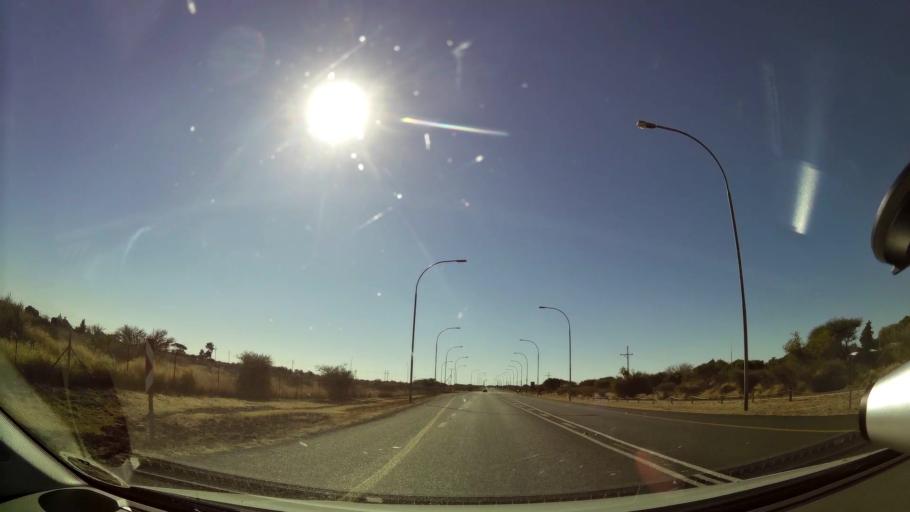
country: ZA
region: Northern Cape
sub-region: Frances Baard District Municipality
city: Warrenton
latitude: -28.1087
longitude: 24.8597
